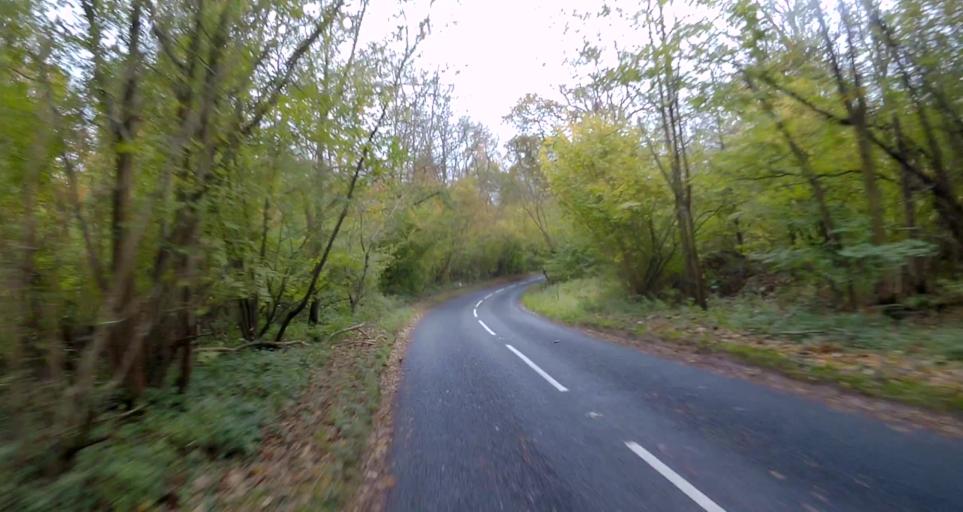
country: GB
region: England
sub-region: Hampshire
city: Four Marks
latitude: 51.1208
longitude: -1.1628
